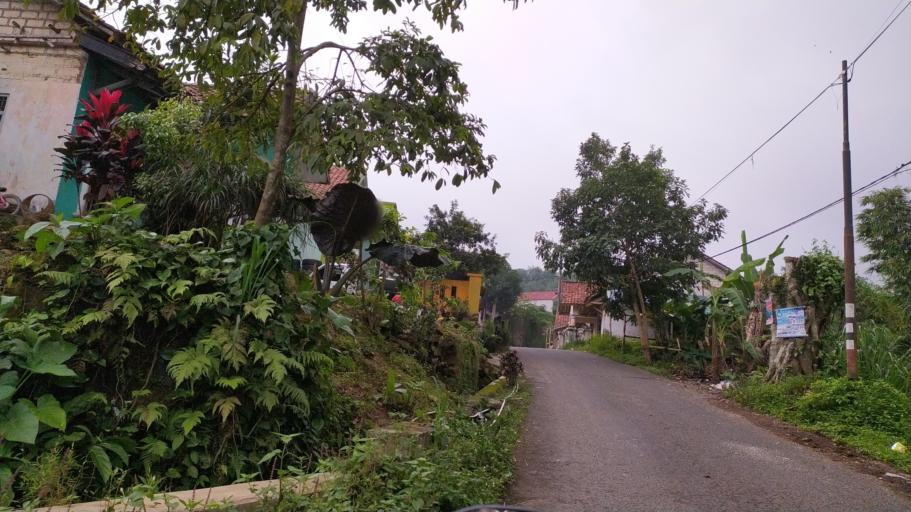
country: ID
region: West Java
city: Bogor
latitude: -6.6550
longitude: 106.7097
